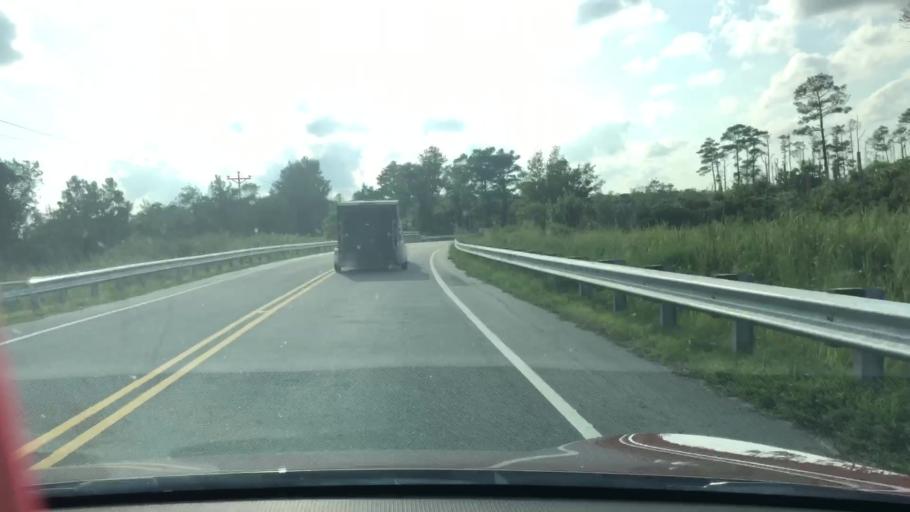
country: US
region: North Carolina
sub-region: Dare County
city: Wanchese
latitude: 35.6075
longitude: -75.8164
